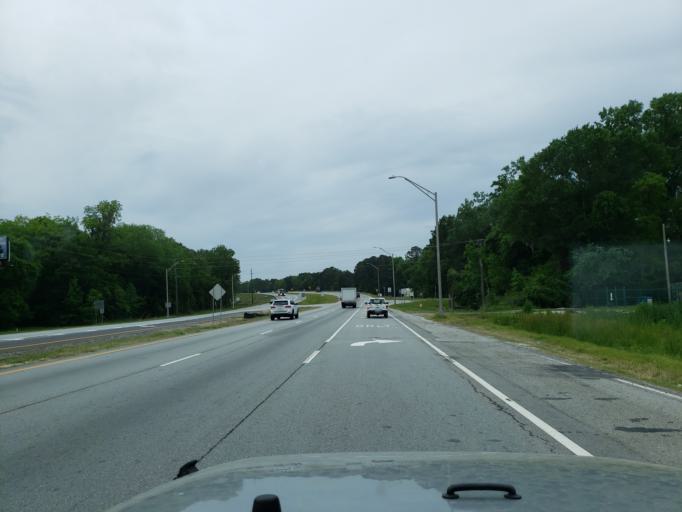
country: US
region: Georgia
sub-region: Chatham County
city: Port Wentworth
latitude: 32.1876
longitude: -81.1935
